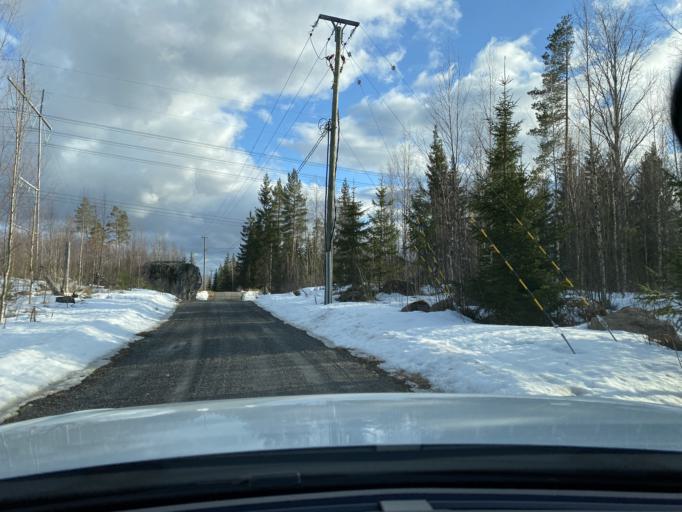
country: FI
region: Pirkanmaa
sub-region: Lounais-Pirkanmaa
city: Mouhijaervi
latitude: 61.4452
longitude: 22.9604
